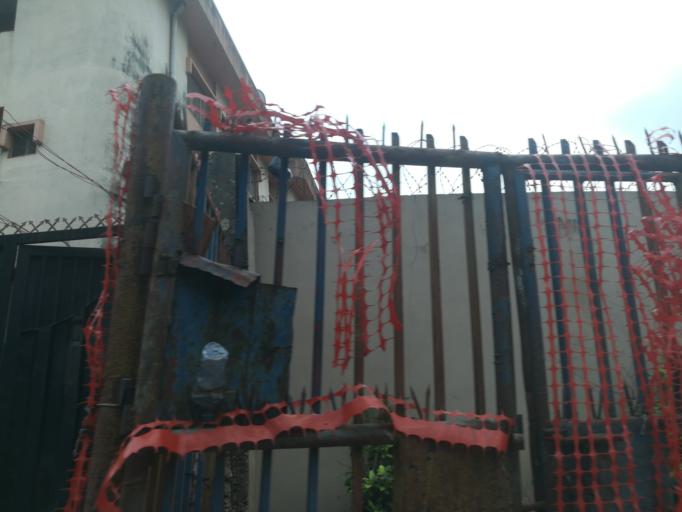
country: NG
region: Lagos
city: Ojota
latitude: 6.6031
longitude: 3.3657
